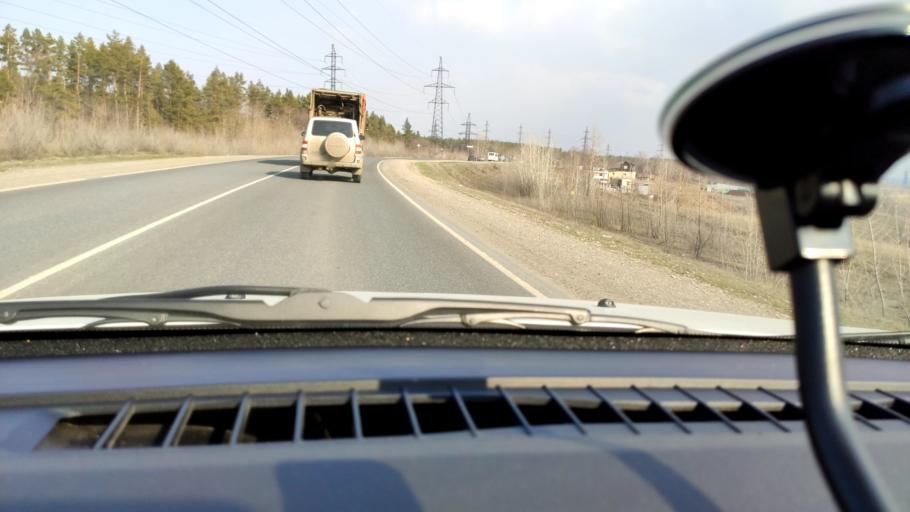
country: RU
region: Samara
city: Samara
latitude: 53.1248
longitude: 50.2022
